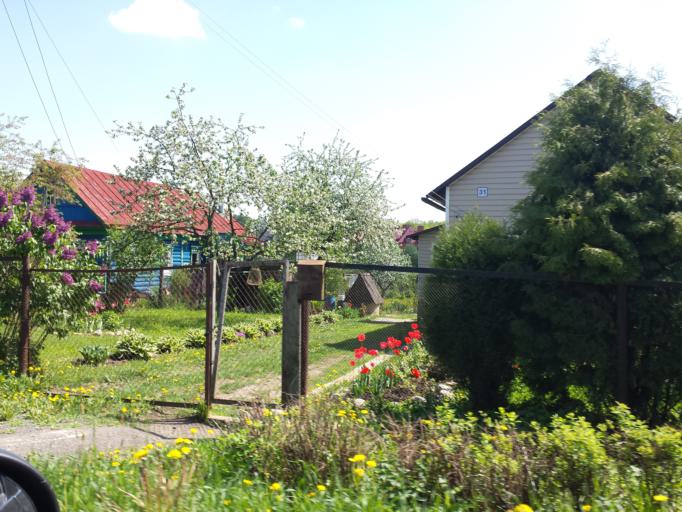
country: RU
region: Moskovskaya
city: Povedniki
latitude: 55.9295
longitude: 37.6196
